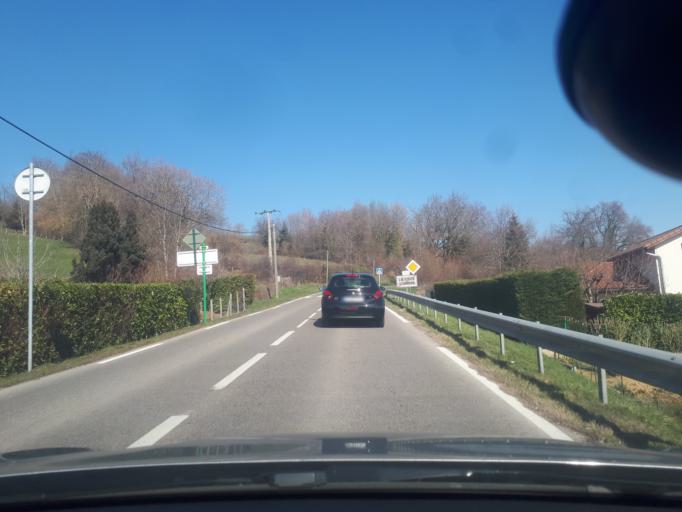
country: FR
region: Rhone-Alpes
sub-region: Departement de l'Isere
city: La Cote-Saint-Andre
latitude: 45.3989
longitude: 5.2719
